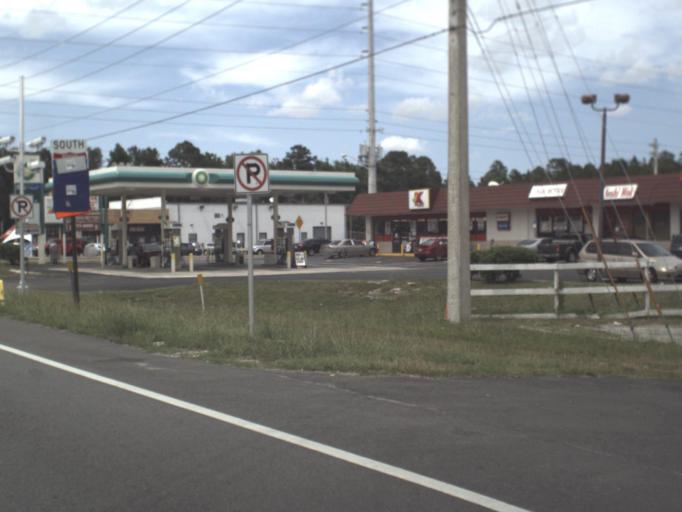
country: US
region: Florida
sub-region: Clay County
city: Bellair-Meadowbrook Terrace
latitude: 30.2036
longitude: -81.7394
